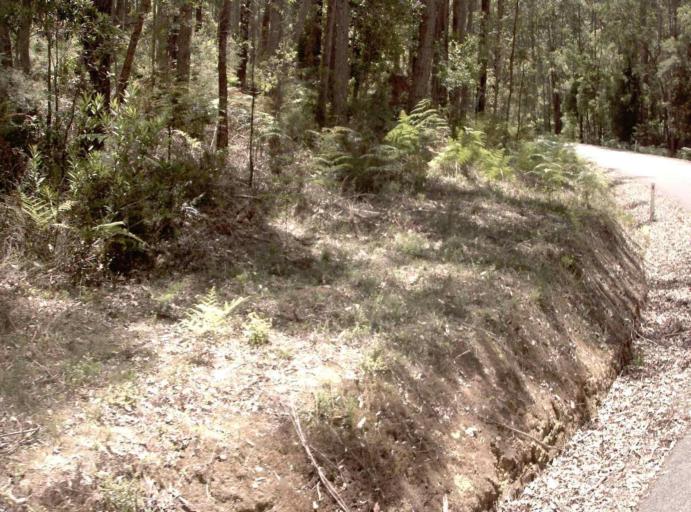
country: AU
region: New South Wales
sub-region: Bombala
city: Bombala
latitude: -37.4866
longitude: 148.9306
